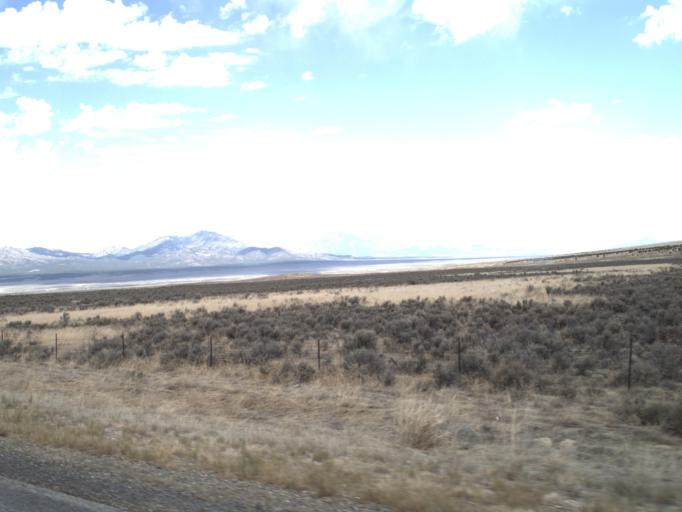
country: US
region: Utah
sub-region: Utah County
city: Eagle Mountain
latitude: 40.0760
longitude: -112.3876
